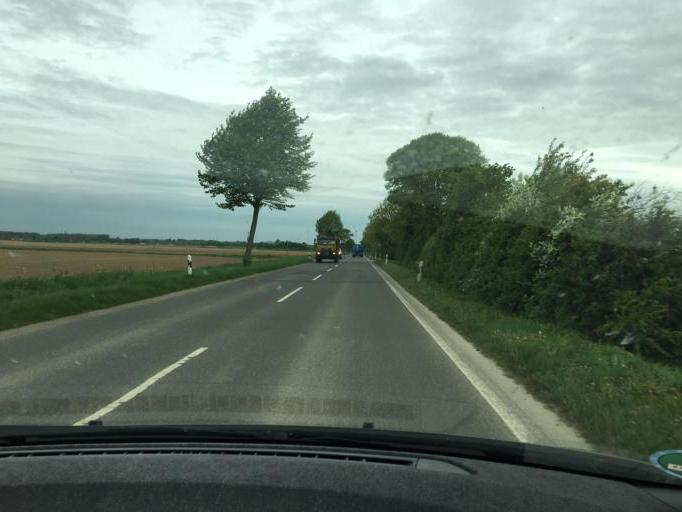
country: DE
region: North Rhine-Westphalia
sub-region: Regierungsbezirk Koln
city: Titz
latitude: 51.0644
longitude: 6.4276
